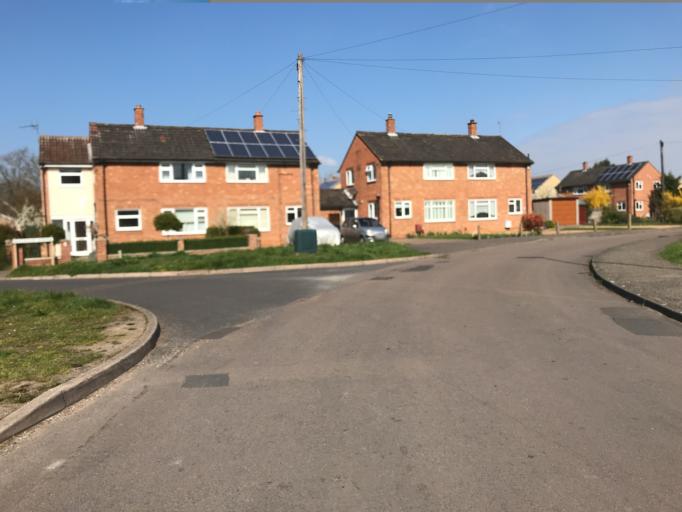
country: GB
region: England
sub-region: Cambridgeshire
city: Sawston
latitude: 52.1529
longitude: 0.1411
